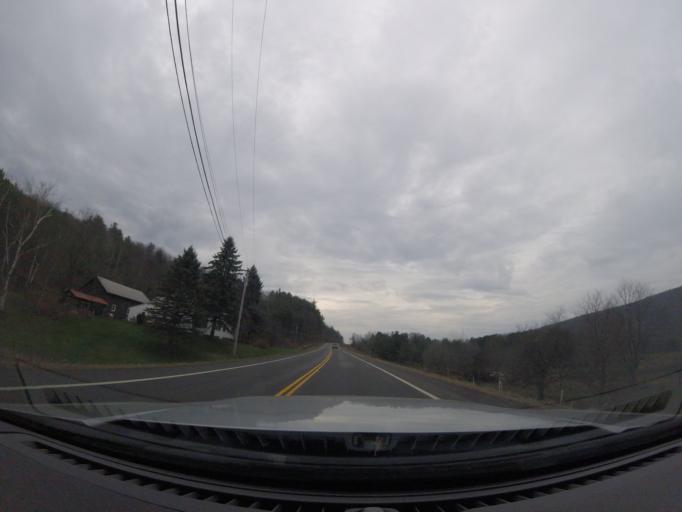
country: US
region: New York
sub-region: Schuyler County
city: Watkins Glen
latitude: 42.4442
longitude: -76.7871
